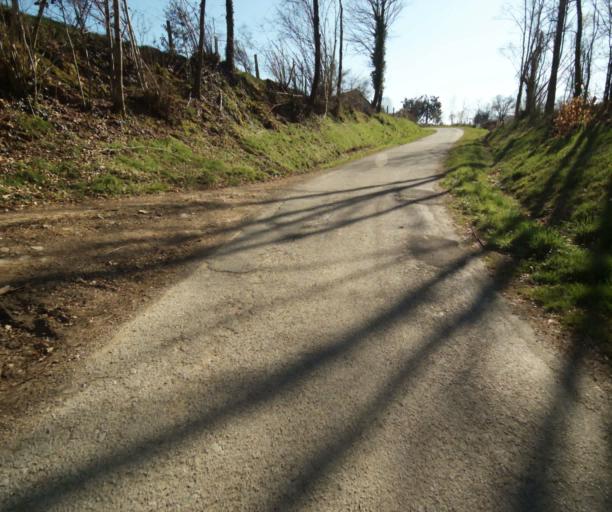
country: FR
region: Limousin
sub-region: Departement de la Correze
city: Chamboulive
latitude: 45.4849
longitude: 1.7000
